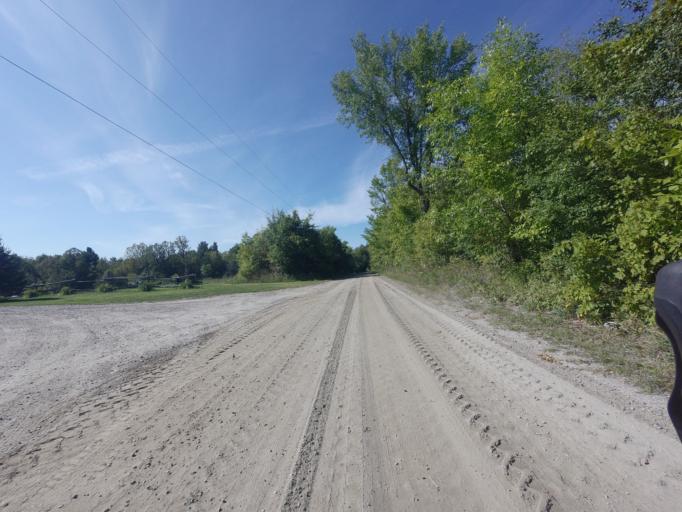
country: CA
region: Ontario
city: Perth
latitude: 44.9370
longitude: -76.3758
